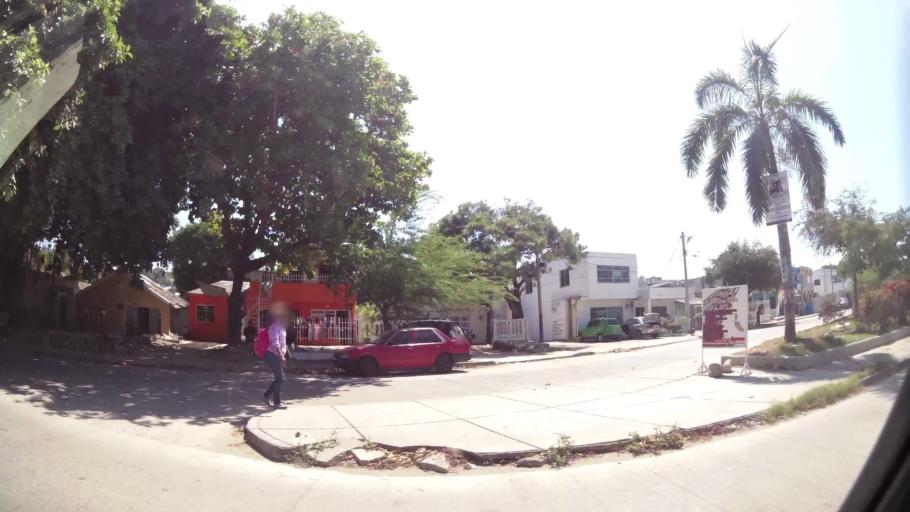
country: CO
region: Bolivar
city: Cartagena
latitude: 10.4349
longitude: -75.5298
